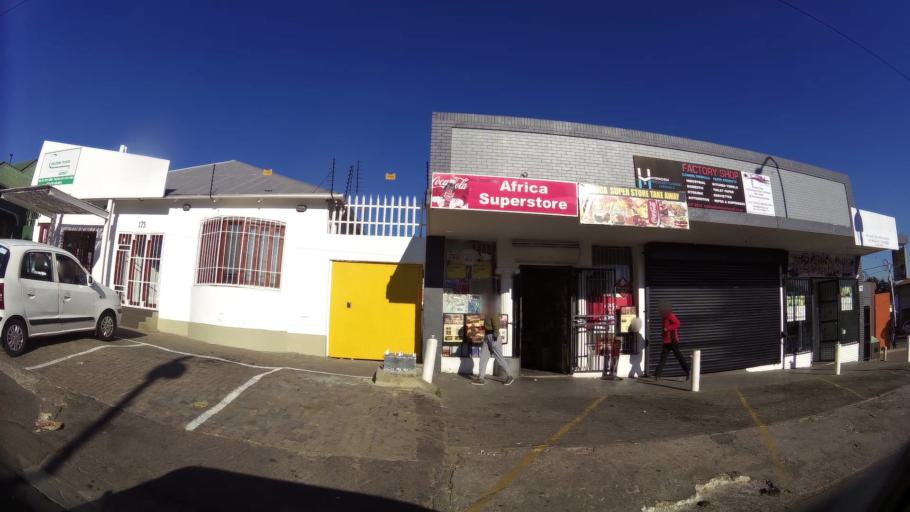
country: ZA
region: Gauteng
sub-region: City of Johannesburg Metropolitan Municipality
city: Johannesburg
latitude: -26.1860
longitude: 28.1065
